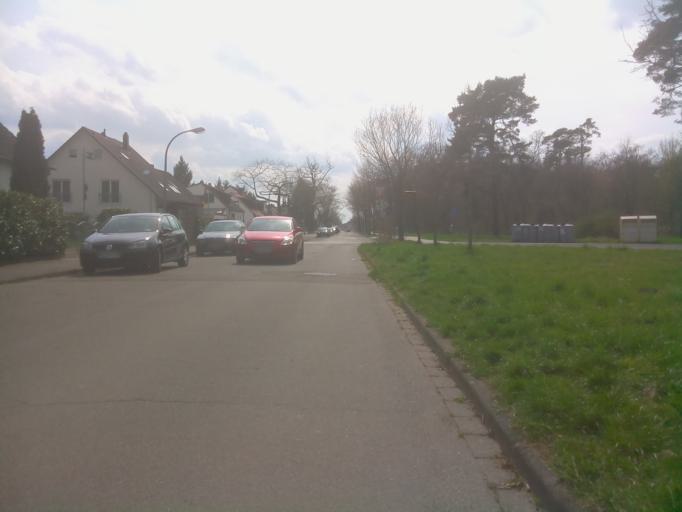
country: DE
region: Baden-Wuerttemberg
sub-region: Karlsruhe Region
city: Mannheim
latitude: 49.5387
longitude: 8.4972
